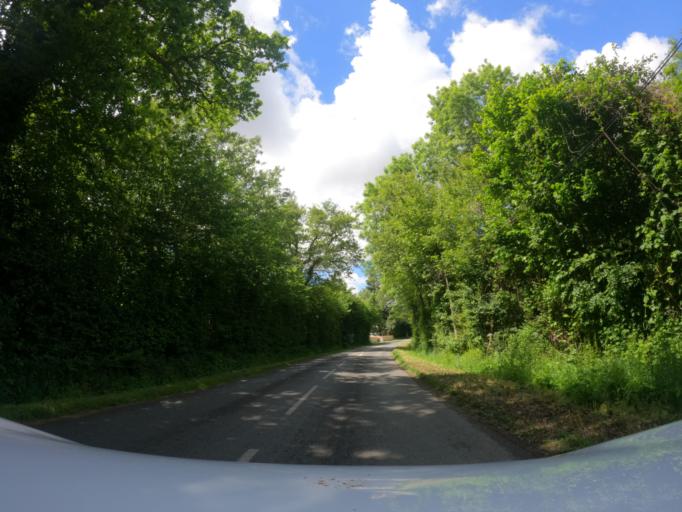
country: FR
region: Pays de la Loire
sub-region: Departement de la Vendee
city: Le Champ-Saint-Pere
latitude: 46.5021
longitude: -1.3492
